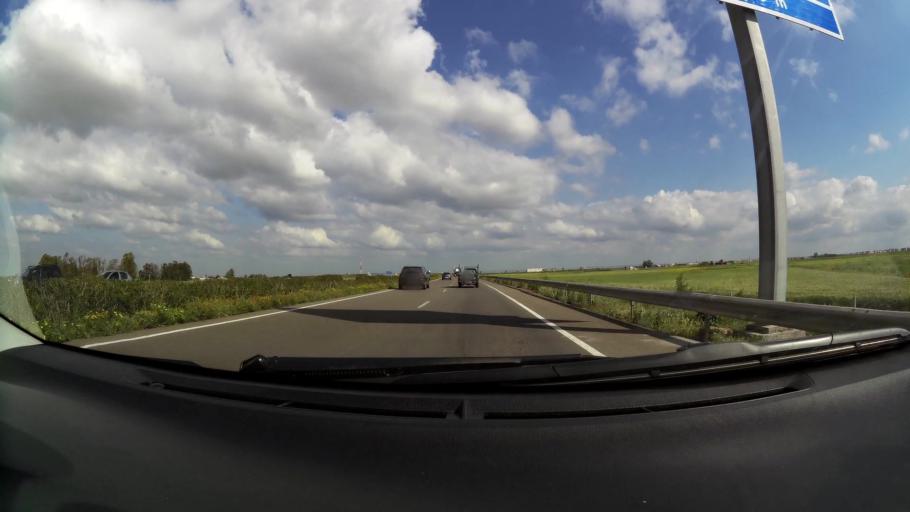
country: MA
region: Chaouia-Ouardigha
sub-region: Settat Province
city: Berrechid
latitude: 33.3053
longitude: -7.5830
